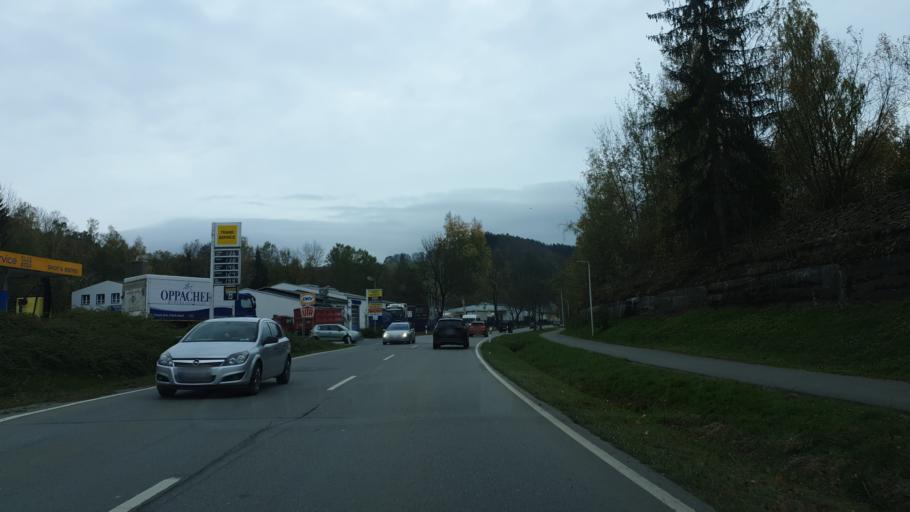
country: DE
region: Saxony
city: Schwarzenberg
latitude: 50.5244
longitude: 12.7896
